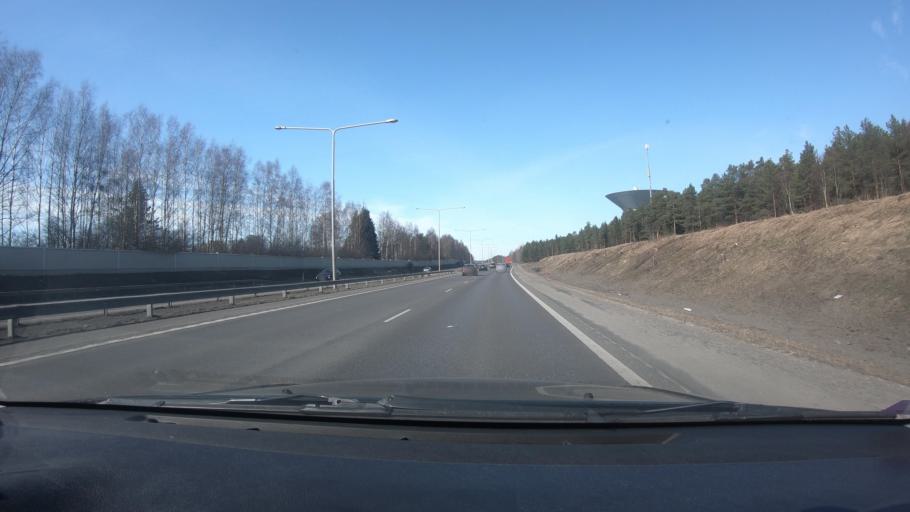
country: FI
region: Northern Ostrobothnia
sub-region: Oulu
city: Oulu
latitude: 65.0343
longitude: 25.4899
